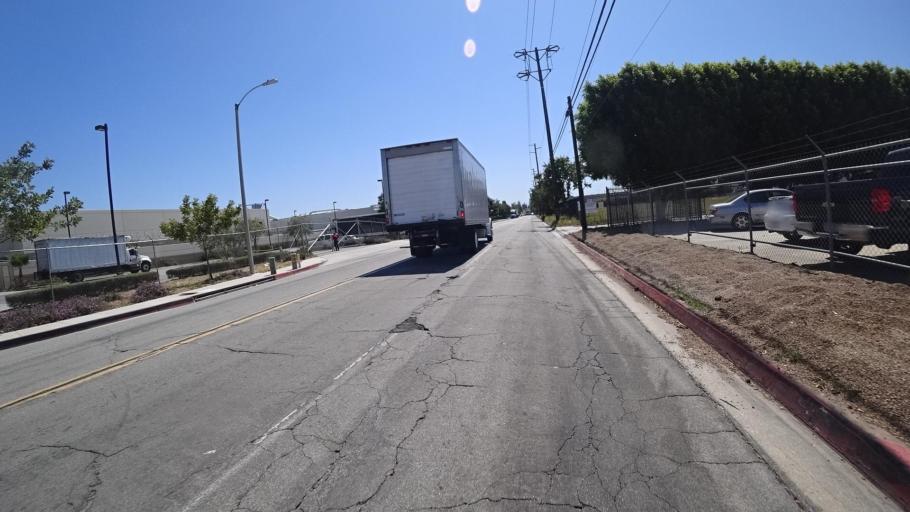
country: US
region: California
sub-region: Los Angeles County
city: Avocado Heights
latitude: 34.0241
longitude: -117.9734
